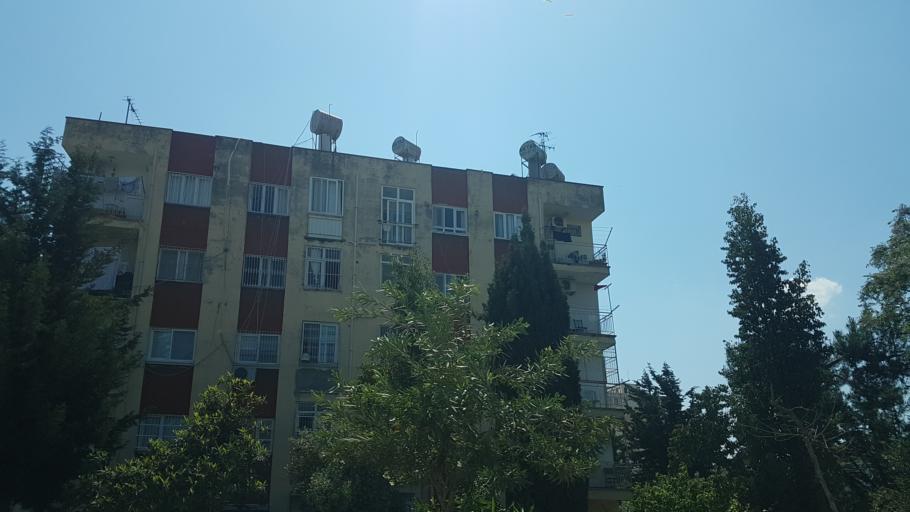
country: TR
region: Adana
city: Adana
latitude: 37.0221
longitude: 35.3705
